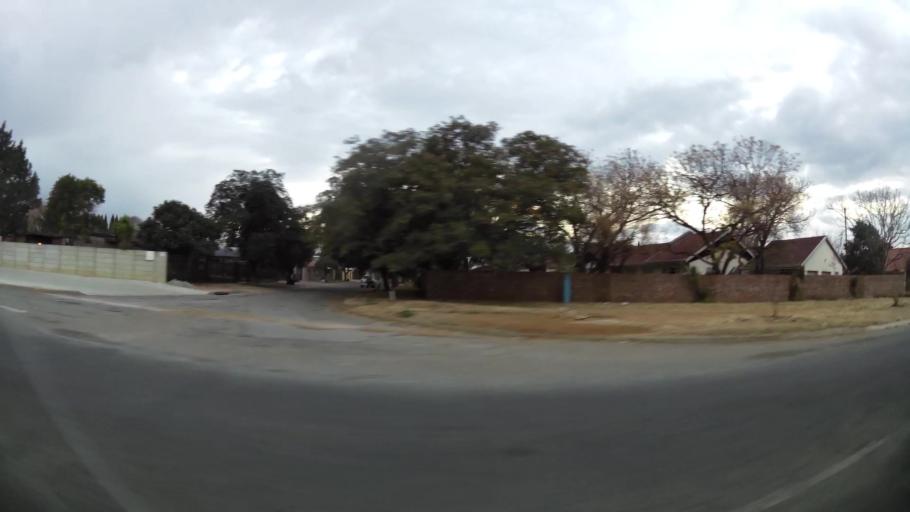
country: ZA
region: Orange Free State
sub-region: Lejweleputswa District Municipality
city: Welkom
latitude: -27.9710
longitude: 26.7247
